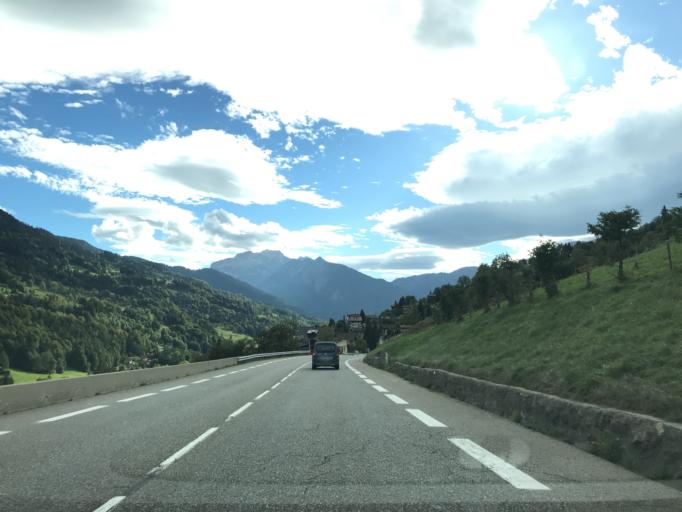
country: FR
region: Rhone-Alpes
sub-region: Departement de la Haute-Savoie
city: Saint-Jean-de-Sixt
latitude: 45.9160
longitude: 6.3779
